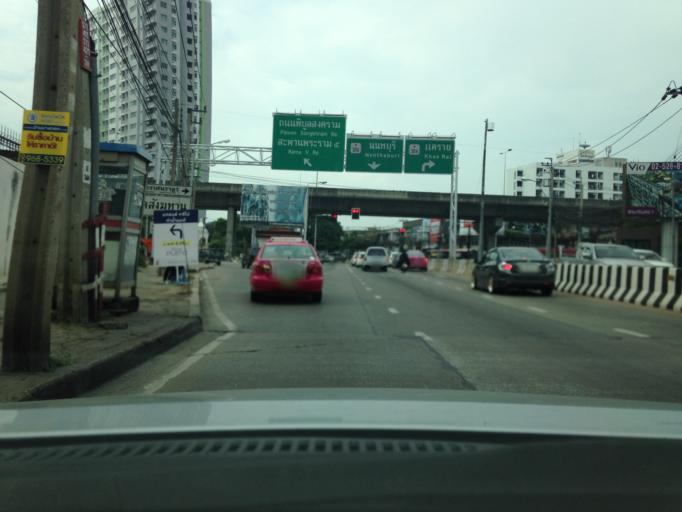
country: TH
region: Nonthaburi
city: Mueang Nonthaburi
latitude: 13.8423
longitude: 100.5114
